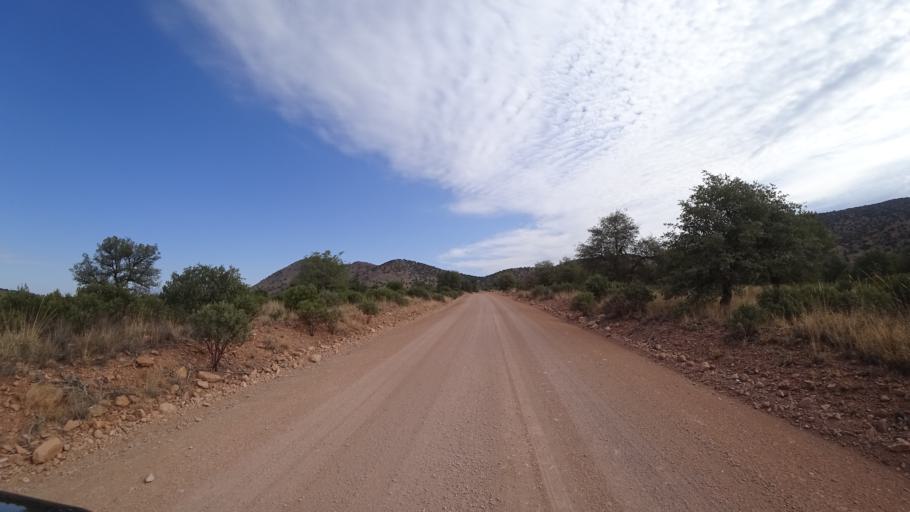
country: MX
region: Sonora
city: Santa Cruz
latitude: 31.4878
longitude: -110.5586
